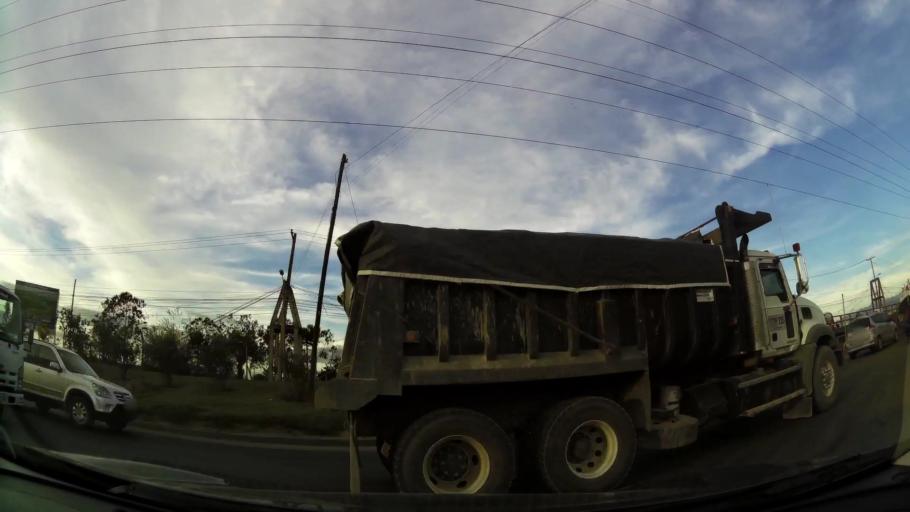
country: CO
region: Cundinamarca
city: Funza
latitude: 4.6961
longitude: -74.1727
